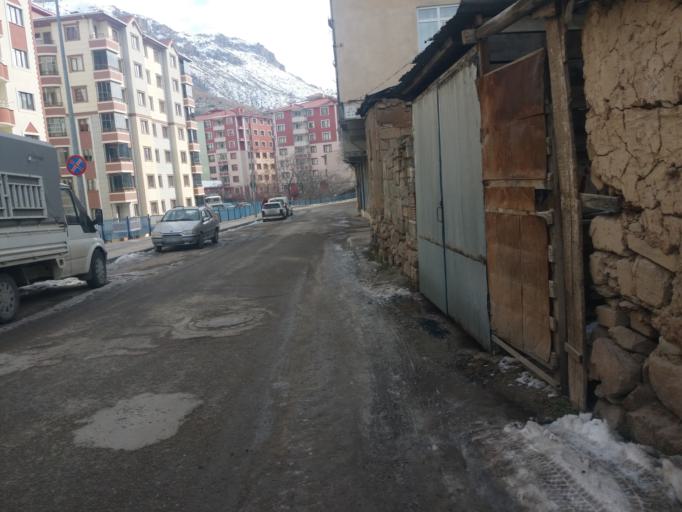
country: TR
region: Gumushane
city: Gumushkhane
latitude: 40.4571
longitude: 39.4855
